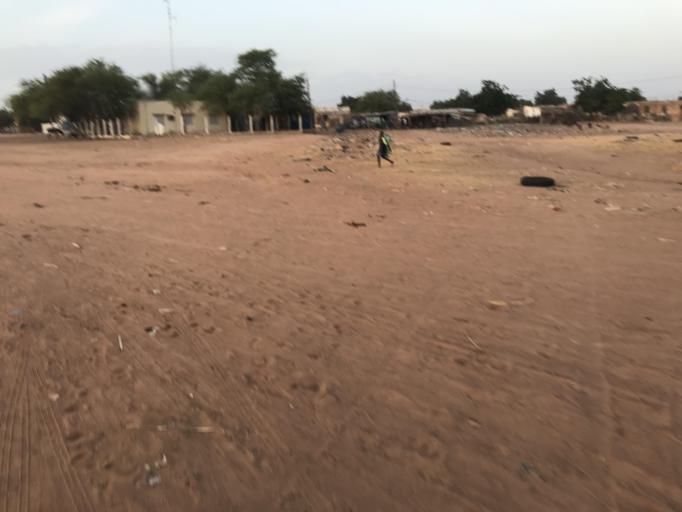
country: SN
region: Matam
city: Ranerou
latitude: 15.2969
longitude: -13.9622
